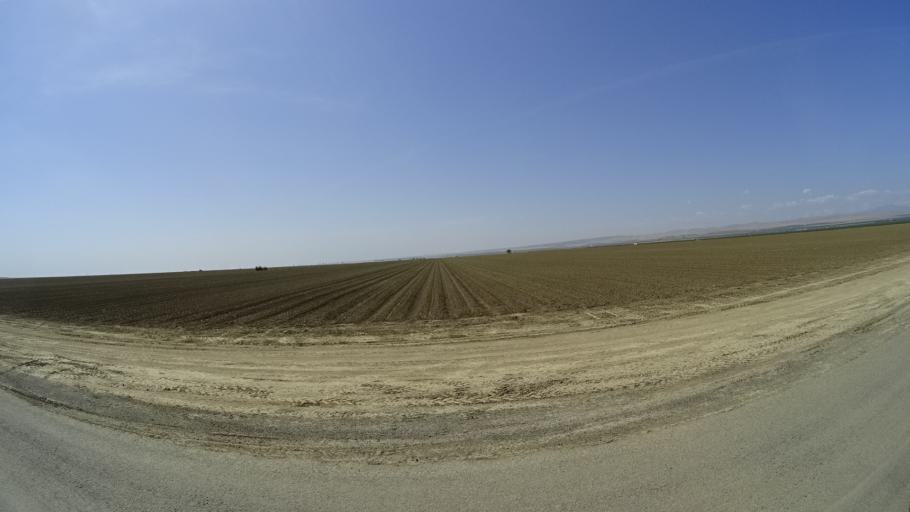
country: US
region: California
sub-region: Kings County
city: Kettleman City
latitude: 36.0942
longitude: -119.9557
